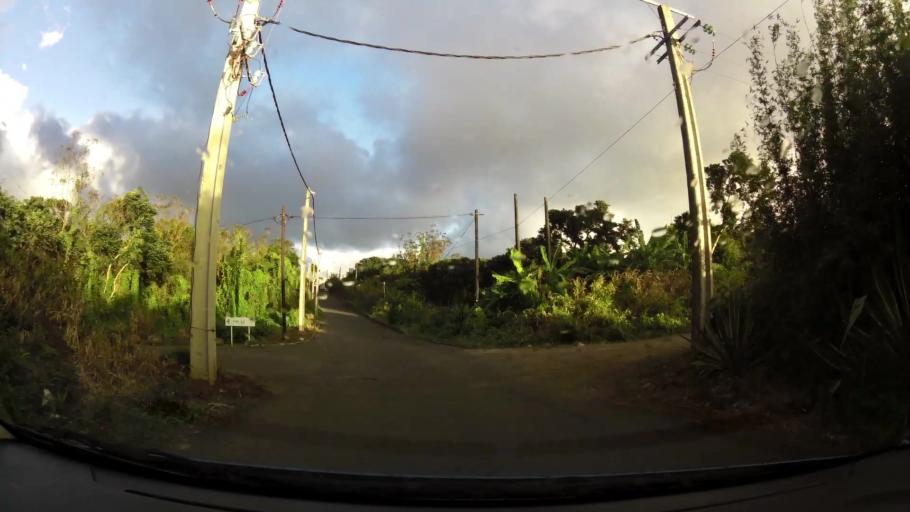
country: MU
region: Plaines Wilhems
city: Curepipe
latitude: -20.3074
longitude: 57.5357
